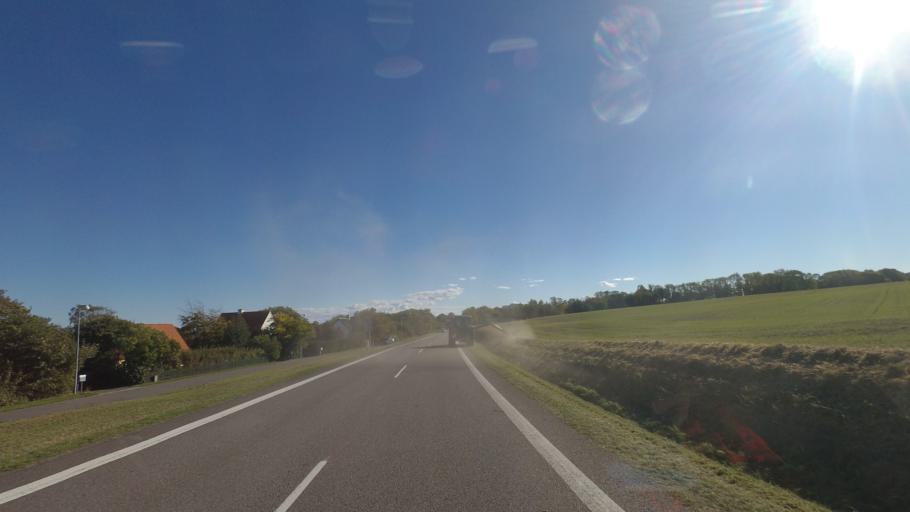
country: DK
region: Capital Region
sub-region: Bornholm Kommune
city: Nexo
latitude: 55.1020
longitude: 15.1440
